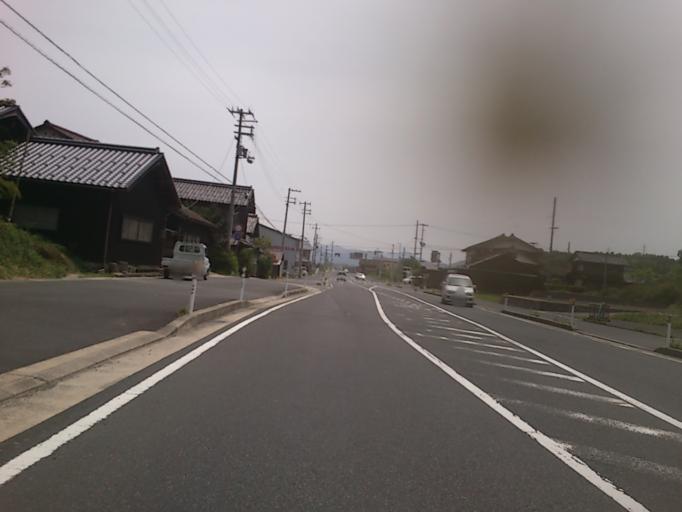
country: JP
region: Kyoto
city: Miyazu
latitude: 35.6303
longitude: 135.0714
